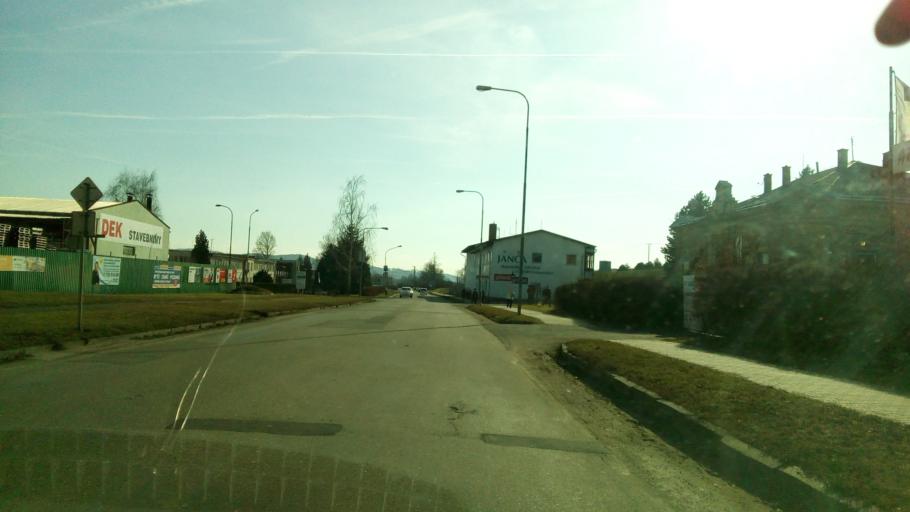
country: CZ
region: Olomoucky
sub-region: Okres Sumperk
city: Sumperk
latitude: 49.9561
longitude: 16.9615
